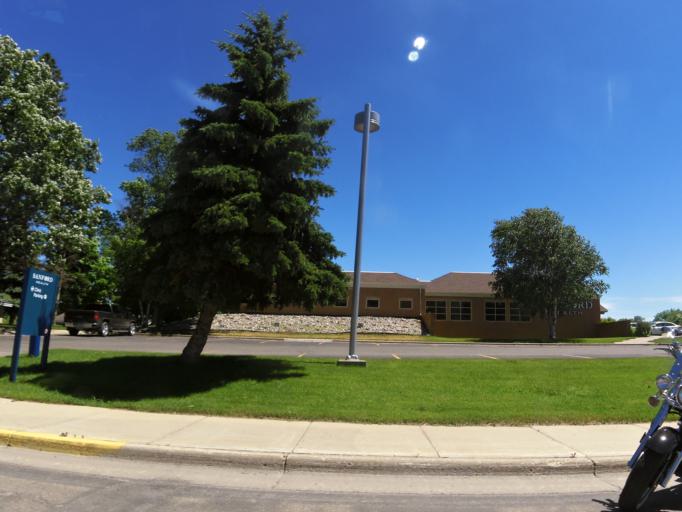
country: US
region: Minnesota
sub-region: Becker County
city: Detroit Lakes
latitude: 46.8098
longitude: -95.8457
